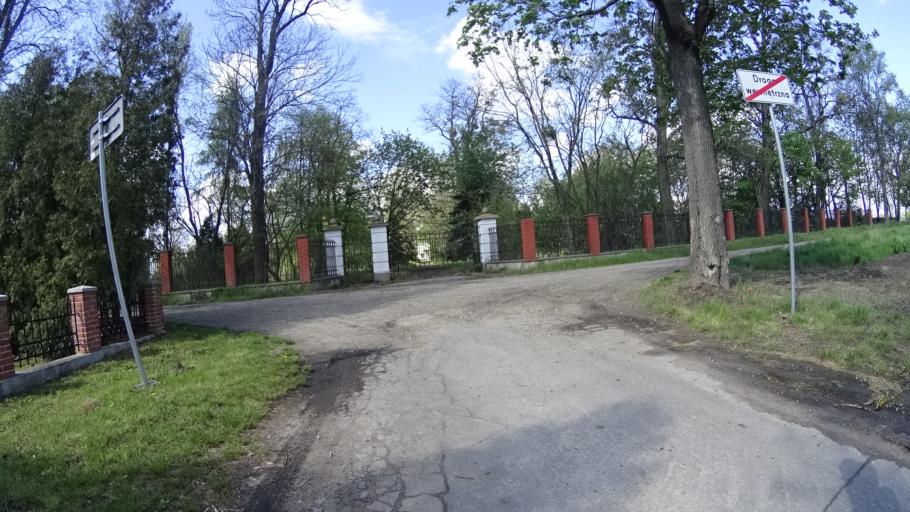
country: PL
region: Masovian Voivodeship
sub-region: Powiat warszawski zachodni
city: Jozefow
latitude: 52.2292
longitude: 20.6939
